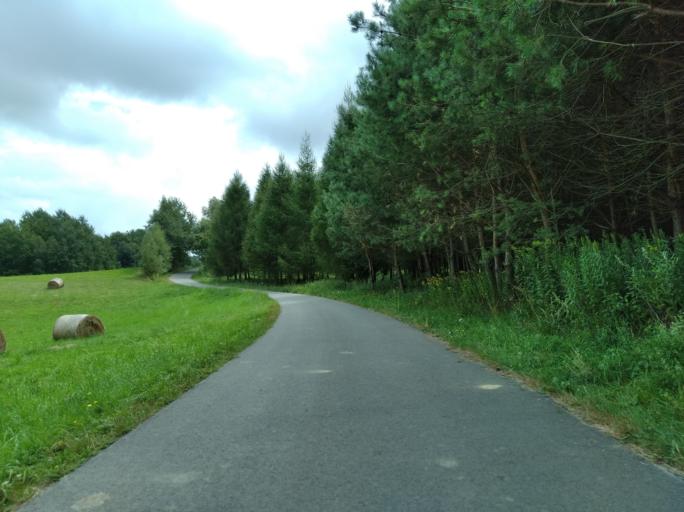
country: PL
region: Subcarpathian Voivodeship
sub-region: Powiat krosnienski
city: Odrzykon
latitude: 49.7770
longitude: 21.7259
